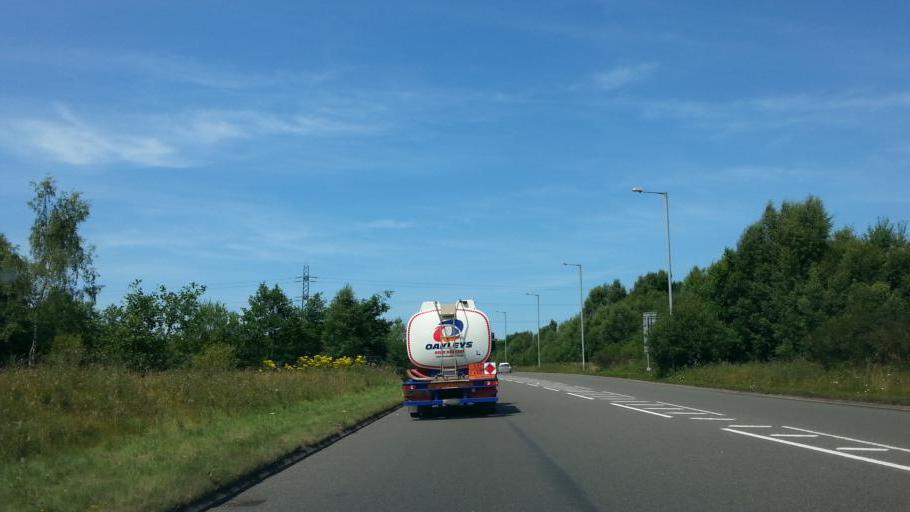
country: GB
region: England
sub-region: Staffordshire
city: Norton Canes
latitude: 52.6769
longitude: -1.9464
